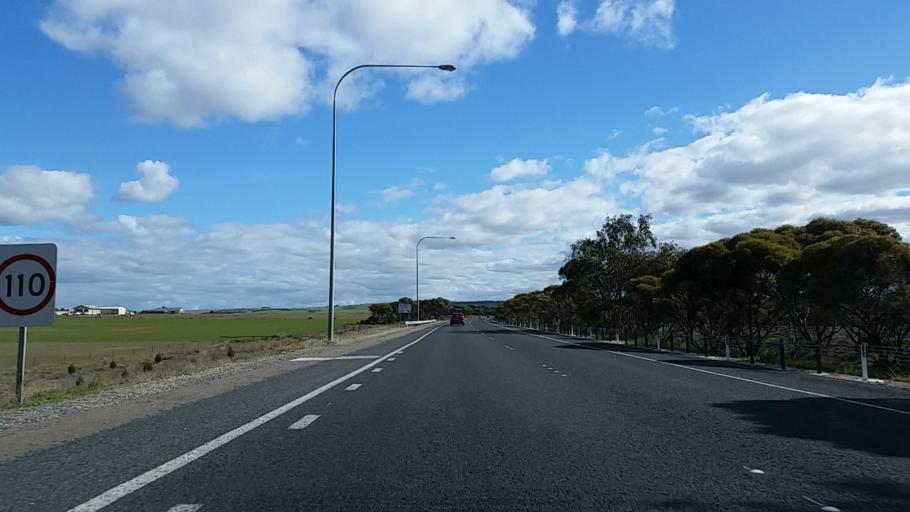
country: AU
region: South Australia
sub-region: Murray Bridge
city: Murray Bridge
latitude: -35.1514
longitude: 139.2805
